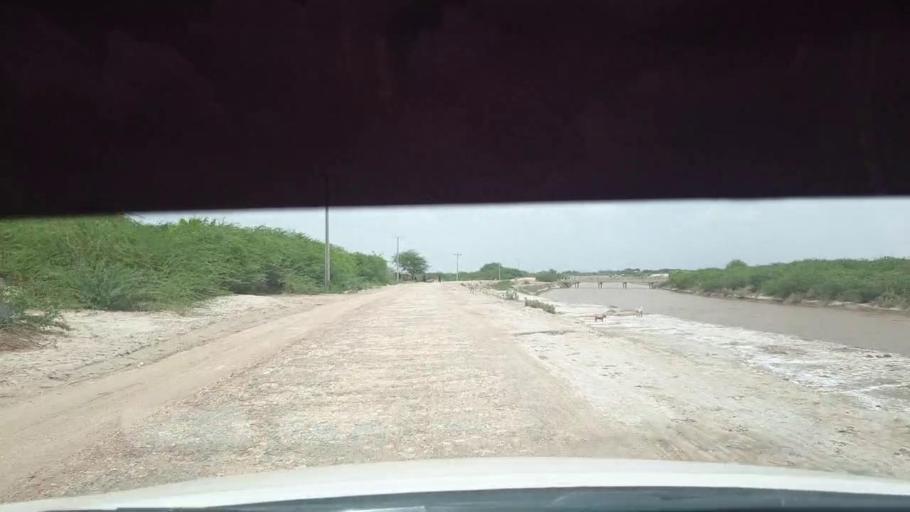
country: PK
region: Sindh
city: Kadhan
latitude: 24.5239
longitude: 69.1228
